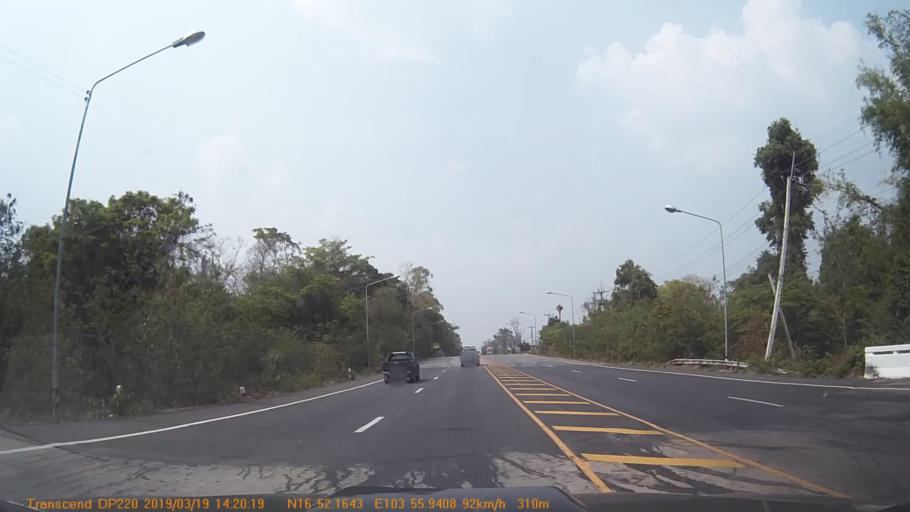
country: TH
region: Sakon Nakhon
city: Phu Phan
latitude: 16.8699
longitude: 103.9323
